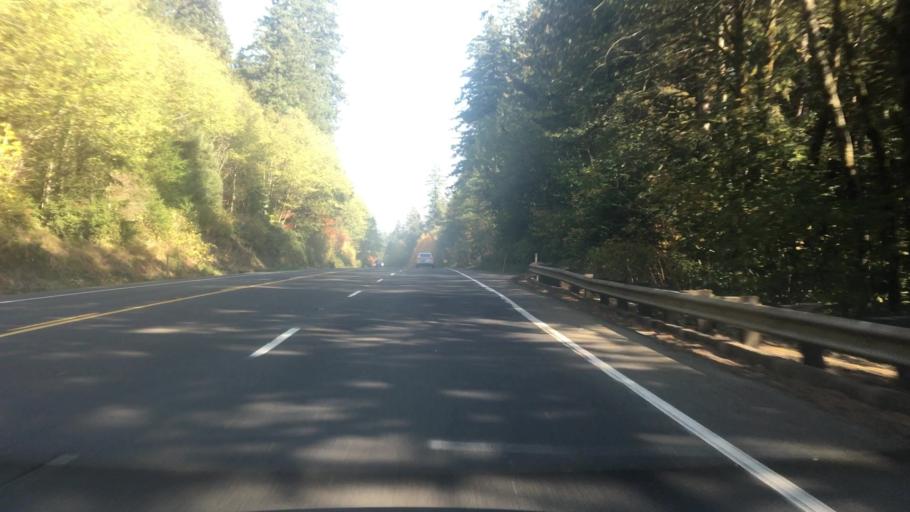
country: US
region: Oregon
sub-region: Lincoln County
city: Rose Lodge
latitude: 45.0487
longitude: -123.7891
